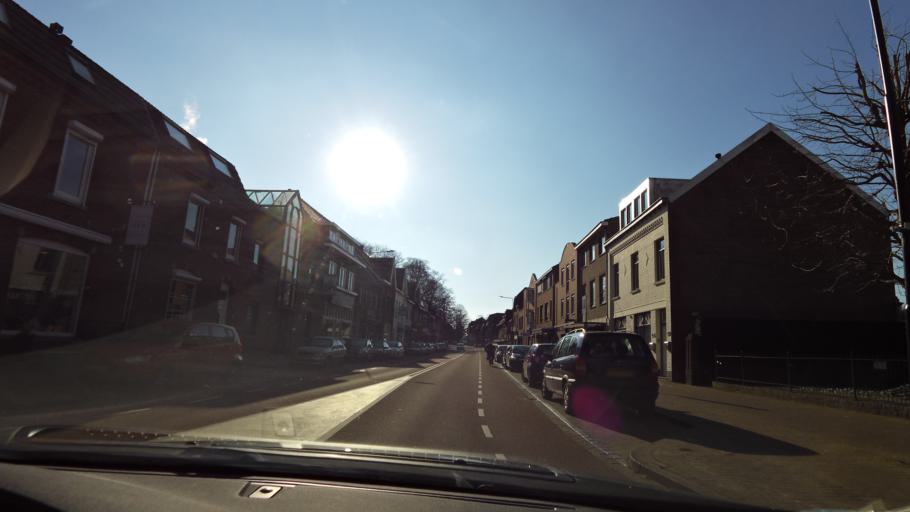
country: NL
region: Limburg
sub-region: Gemeente Schinnen
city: Amstenrade
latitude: 50.9419
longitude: 5.9234
